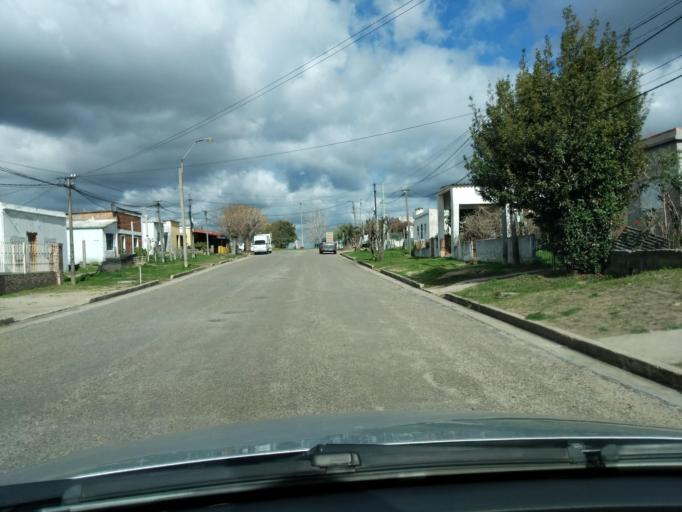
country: UY
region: Florida
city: Florida
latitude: -34.0896
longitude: -56.2283
